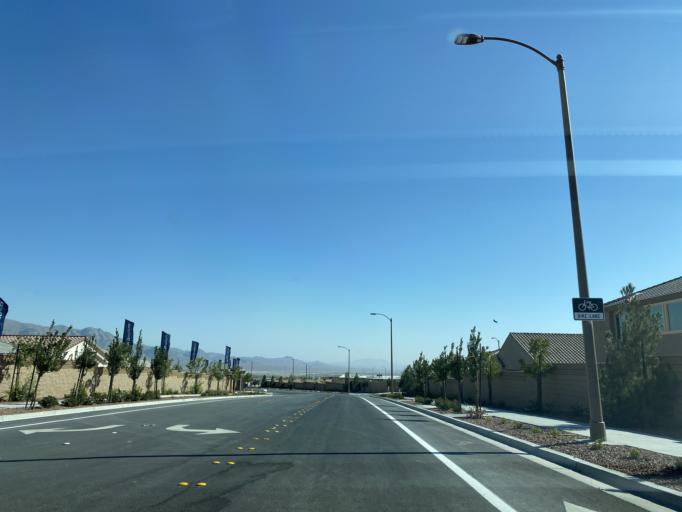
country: US
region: Nevada
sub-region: Clark County
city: Summerlin South
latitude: 36.3166
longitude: -115.3145
